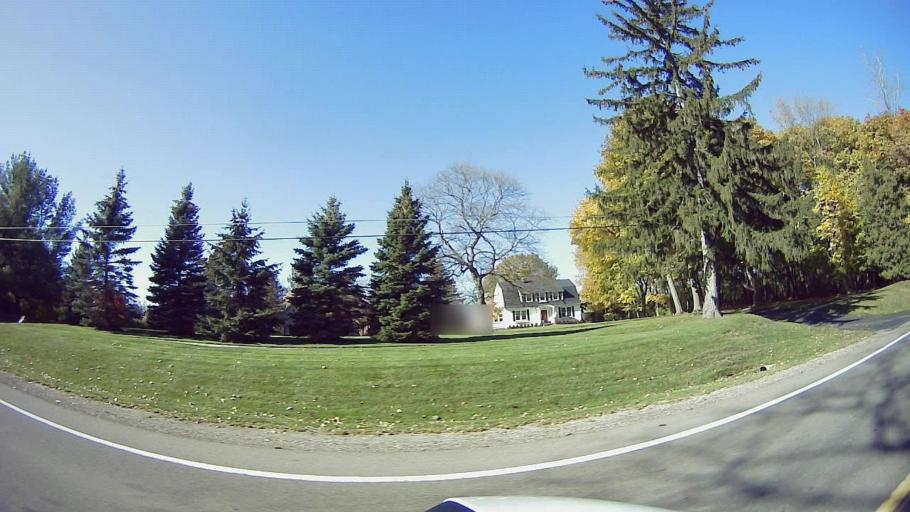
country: US
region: Michigan
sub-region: Oakland County
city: Farmington Hills
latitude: 42.4909
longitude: -83.3779
